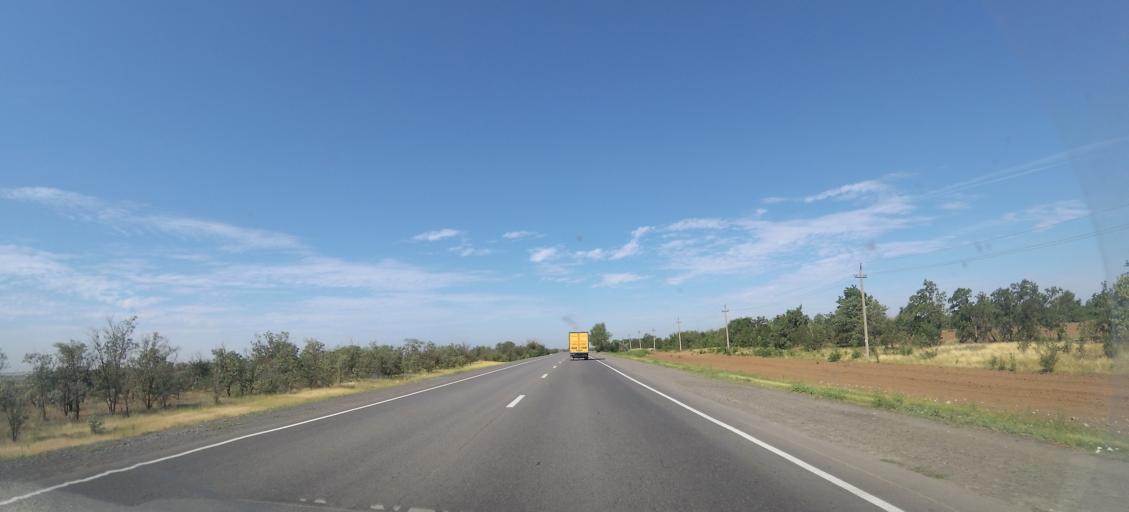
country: RU
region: Volgograd
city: Oktyabr'skiy
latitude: 48.6956
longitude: 43.7944
